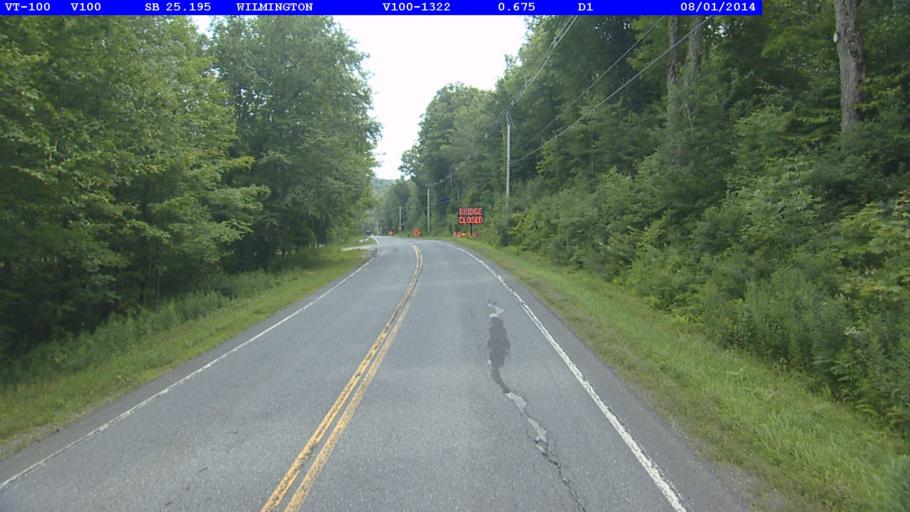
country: US
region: Vermont
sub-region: Windham County
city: Dover
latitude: 42.8369
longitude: -72.8564
